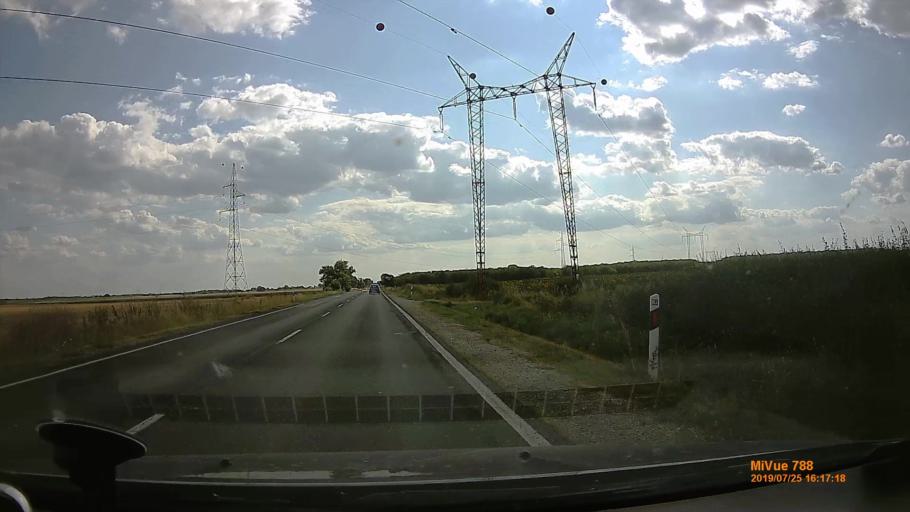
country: HU
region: Heves
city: Kal
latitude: 47.7705
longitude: 20.2775
